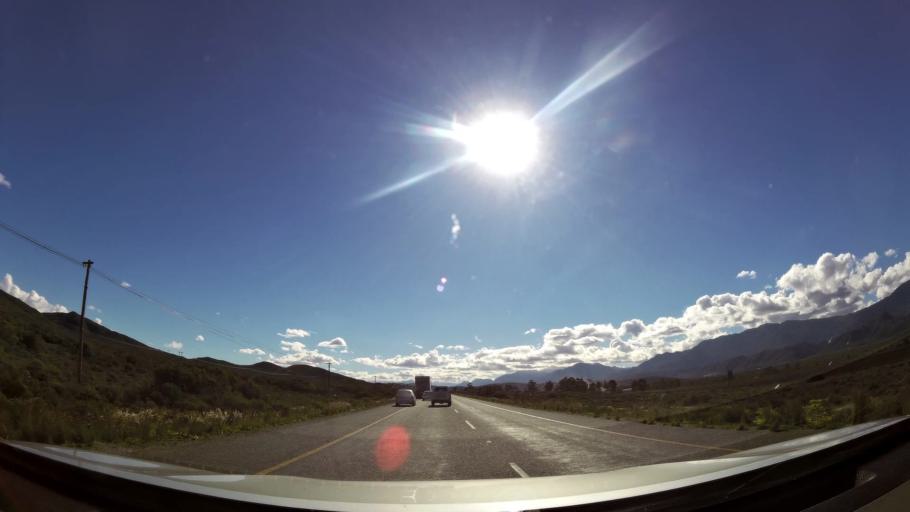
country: ZA
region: Western Cape
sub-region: Cape Winelands District Municipality
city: Ashton
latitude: -33.7671
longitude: 19.7460
